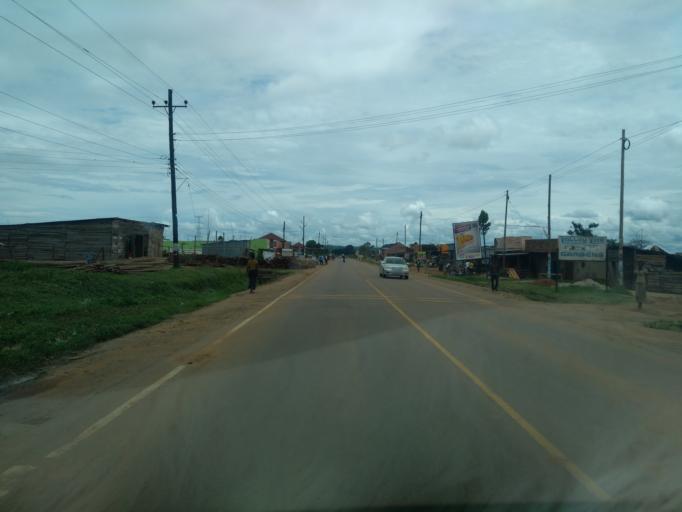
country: UG
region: Central Region
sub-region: Butambala District
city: Gombe
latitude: -0.0140
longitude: 32.0302
